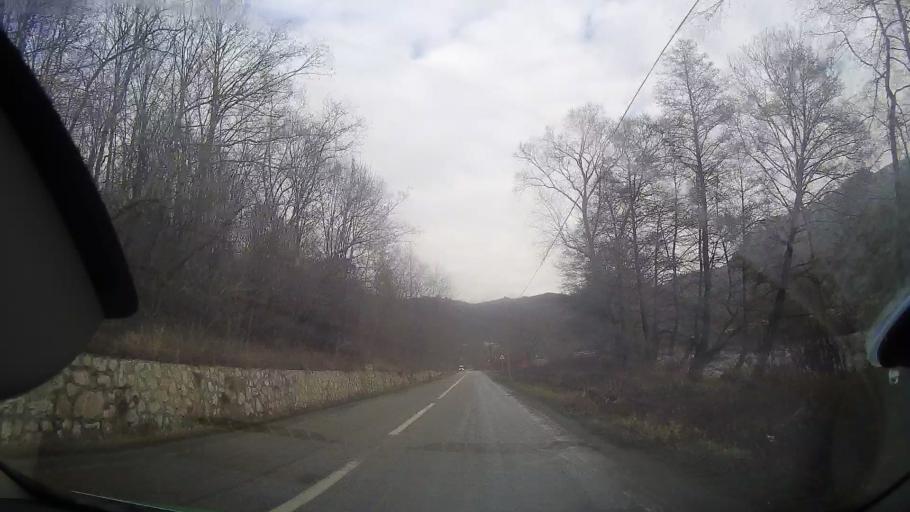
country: RO
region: Alba
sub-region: Comuna Ocolis
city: Ocolis
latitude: 46.4395
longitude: 23.4530
